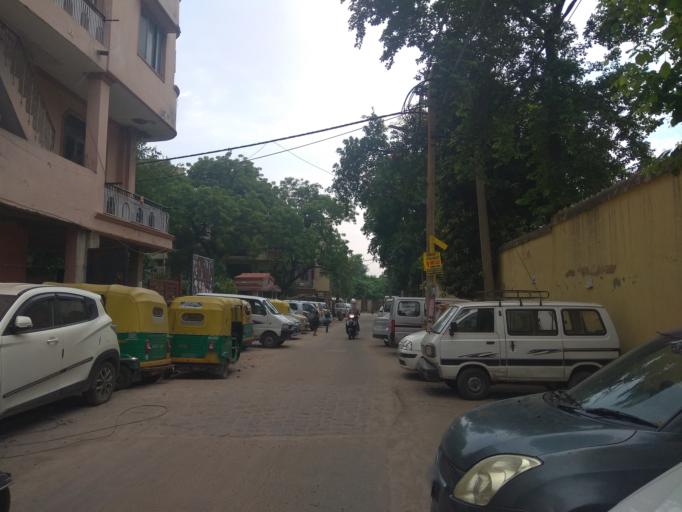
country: IN
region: NCT
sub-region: New Delhi
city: New Delhi
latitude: 28.5728
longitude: 77.2530
